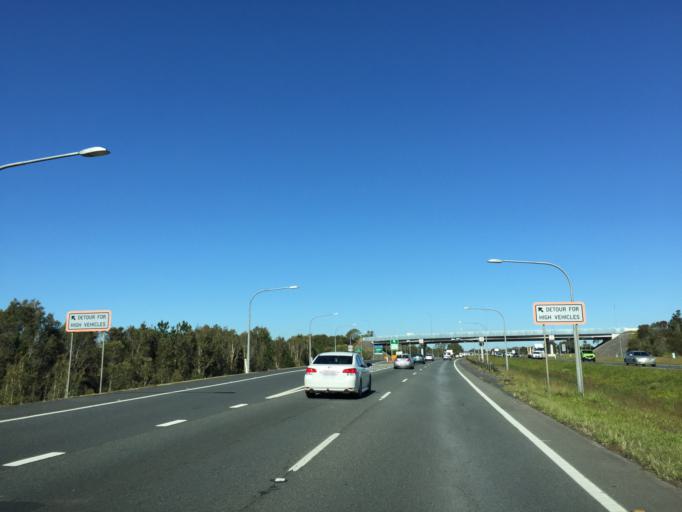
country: AU
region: Queensland
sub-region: Moreton Bay
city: Caboolture
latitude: -27.0690
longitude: 152.9777
